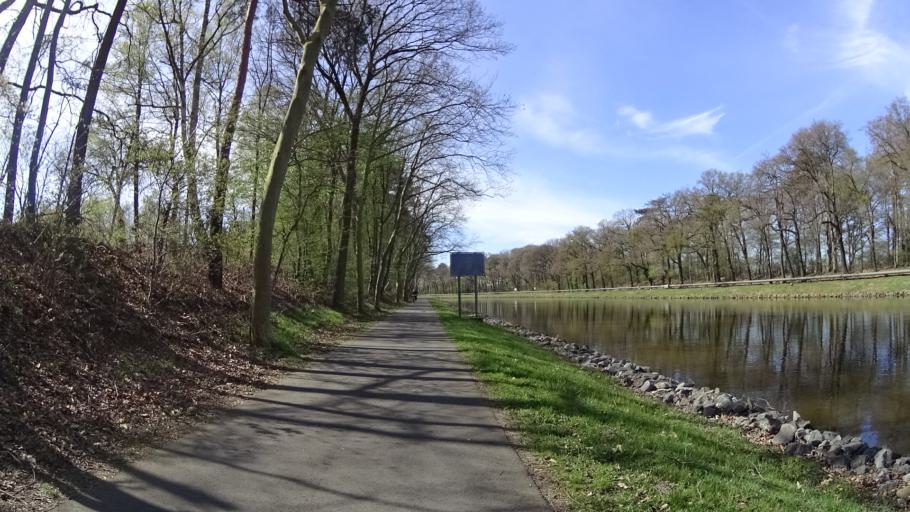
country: DE
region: Lower Saxony
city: Lingen
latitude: 52.5569
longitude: 7.2972
